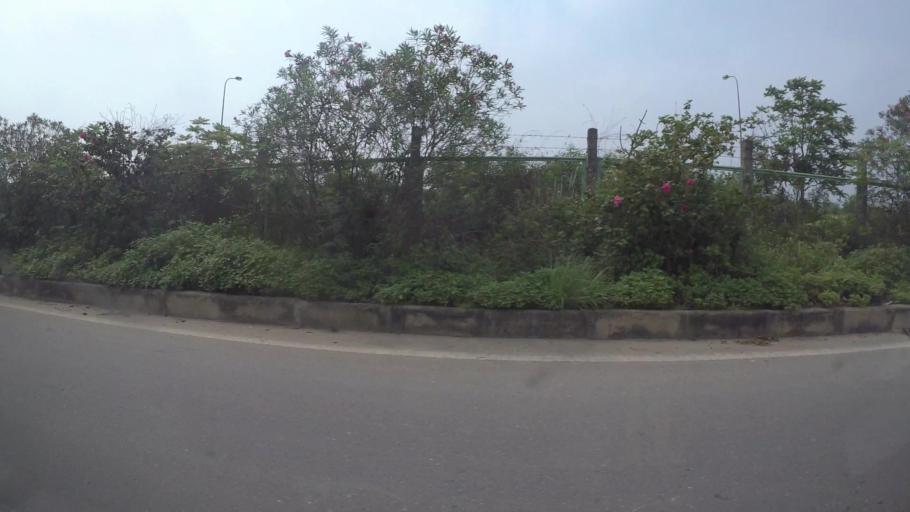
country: VN
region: Ha Noi
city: Lien Quan
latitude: 20.9900
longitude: 105.5637
